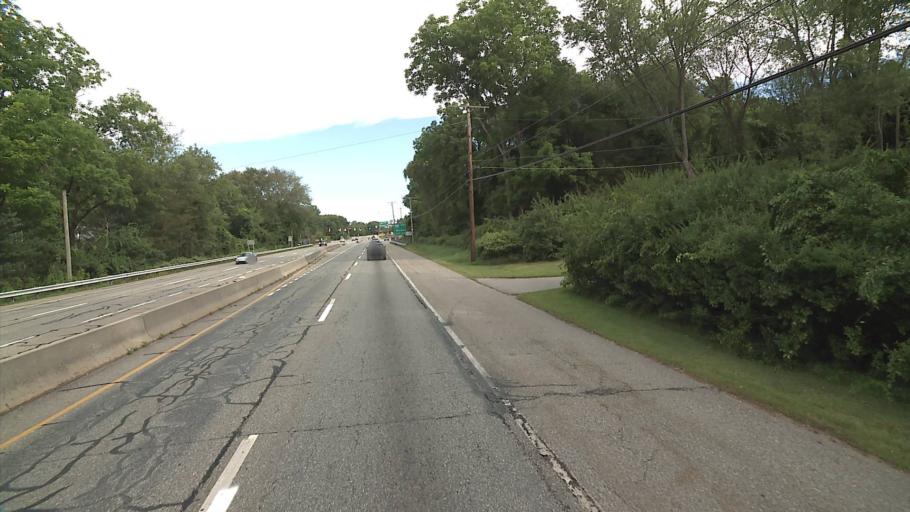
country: US
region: Connecticut
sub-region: New London County
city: Uncasville
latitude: 41.4125
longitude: -72.1080
